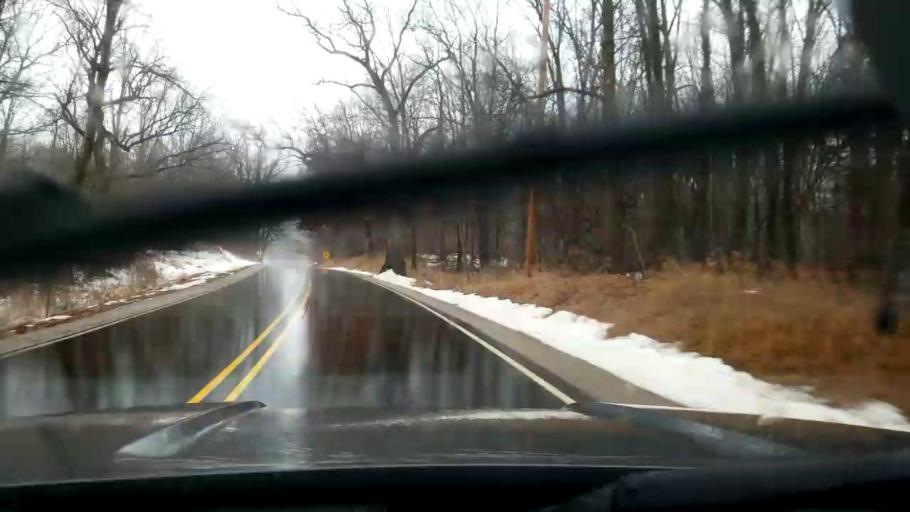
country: US
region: Michigan
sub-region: Jackson County
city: Grass Lake
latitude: 42.3244
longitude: -84.2209
